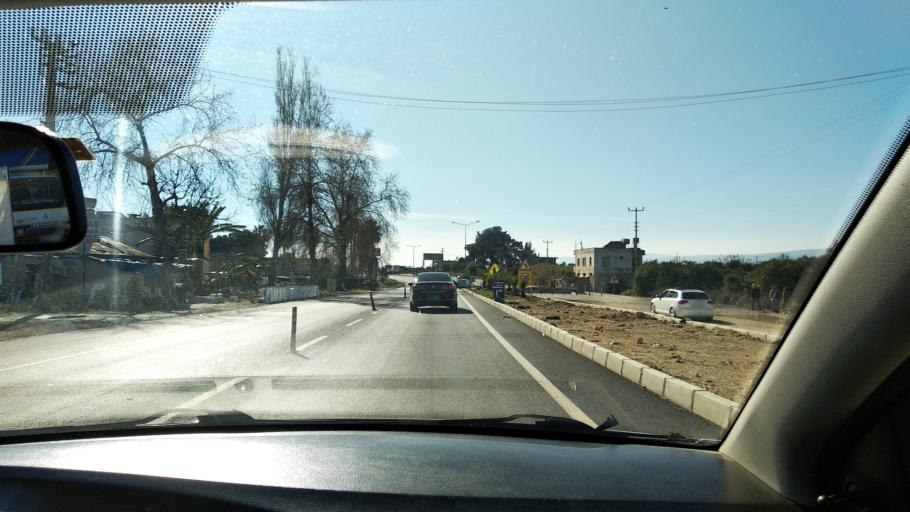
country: TR
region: Mersin
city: Tomuk
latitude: 36.6674
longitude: 34.4014
